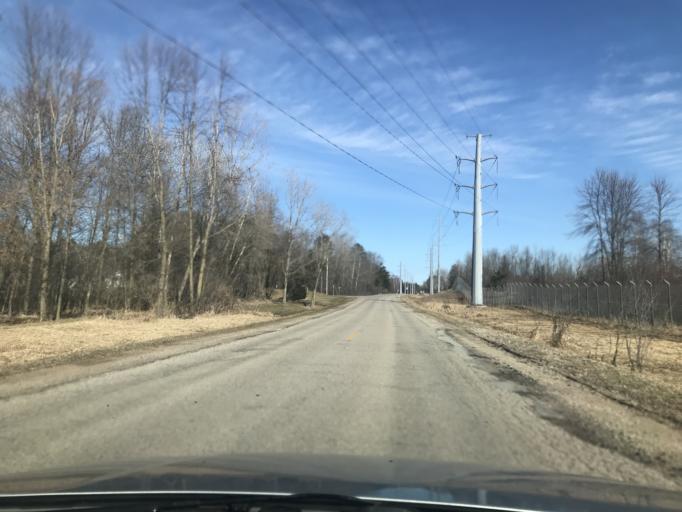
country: US
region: Michigan
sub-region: Menominee County
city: Menominee
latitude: 45.1445
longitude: -87.6279
